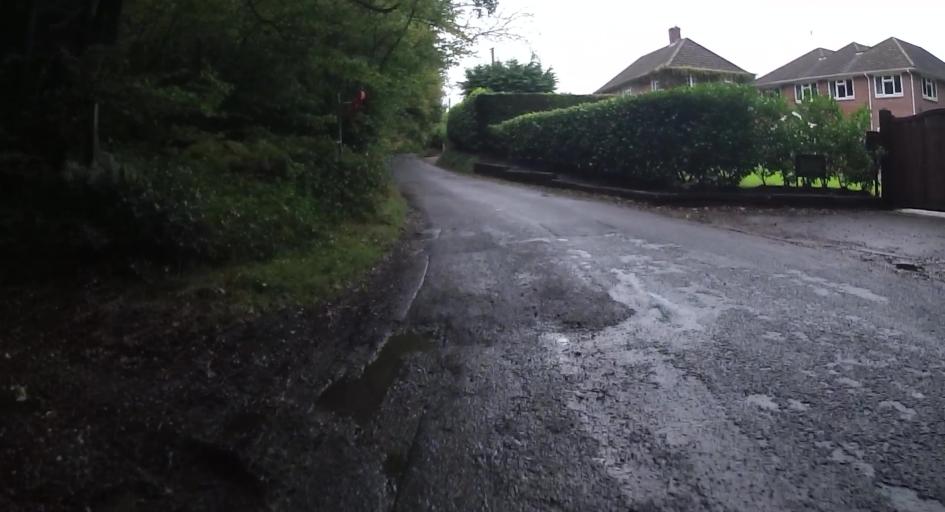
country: GB
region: England
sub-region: West Berkshire
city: Thatcham
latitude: 51.4181
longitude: -1.1795
